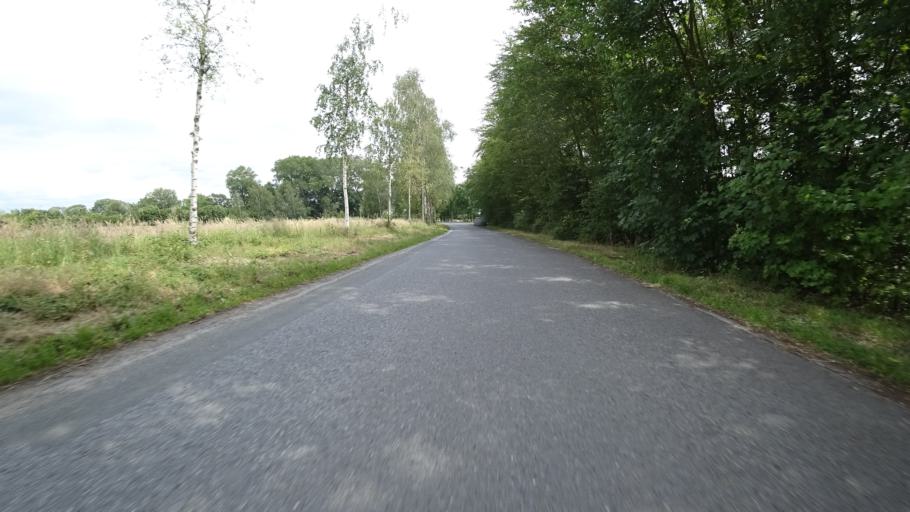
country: DE
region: North Rhine-Westphalia
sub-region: Regierungsbezirk Detmold
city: Rheda-Wiedenbruck
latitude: 51.8679
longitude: 8.3165
